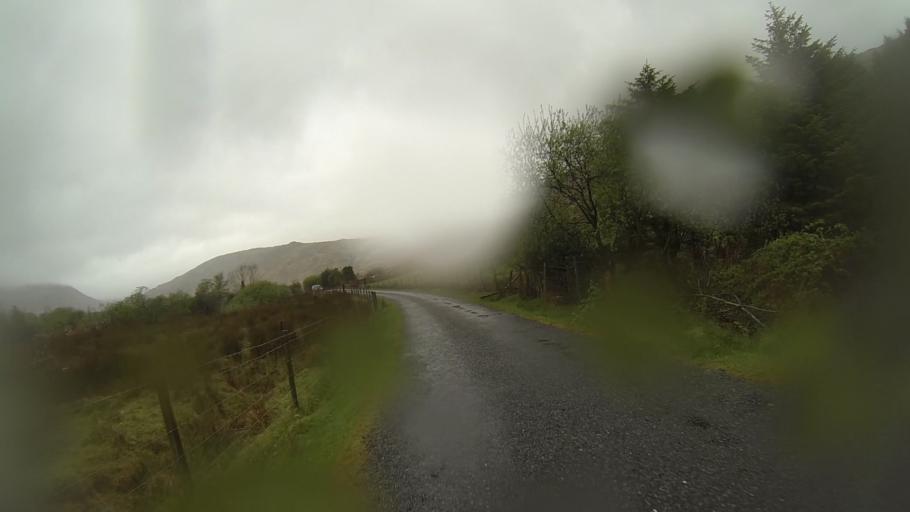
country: IE
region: Munster
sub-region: Ciarrai
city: Kenmare
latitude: 51.9506
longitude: -9.6785
